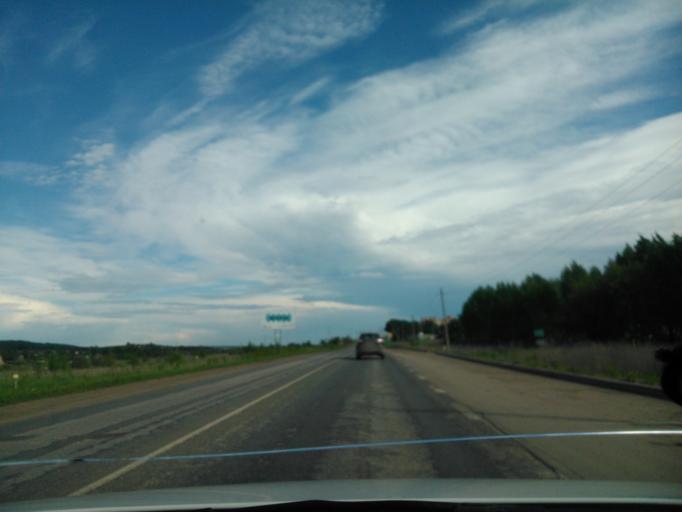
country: RU
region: Perm
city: Lobanovo
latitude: 57.8702
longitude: 56.2843
